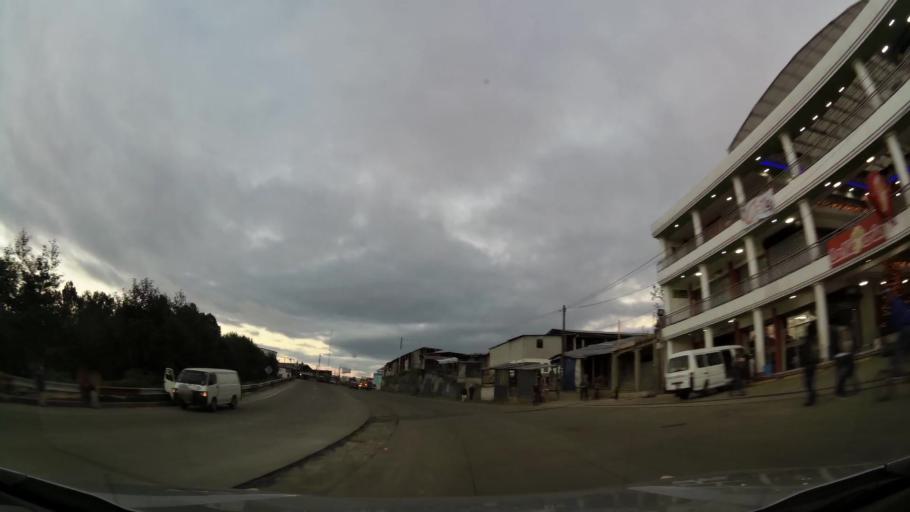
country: GT
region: Quiche
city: Chichicastenango
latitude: 14.8557
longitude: -91.0613
